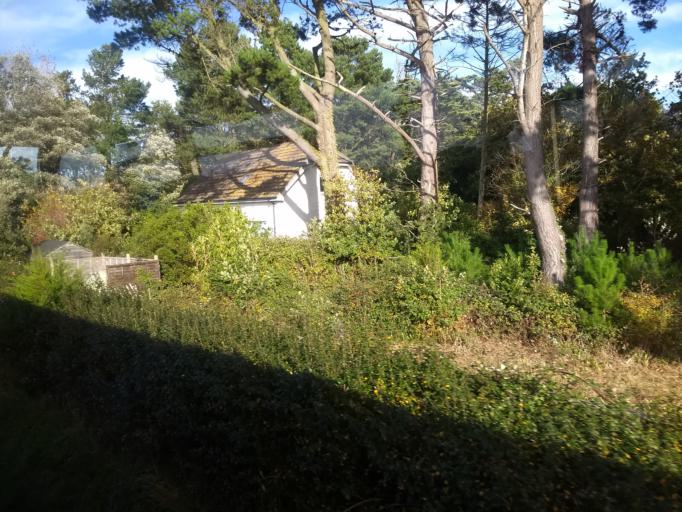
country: GB
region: England
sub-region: Isle of Wight
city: Yarmouth
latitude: 50.7050
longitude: -1.4859
